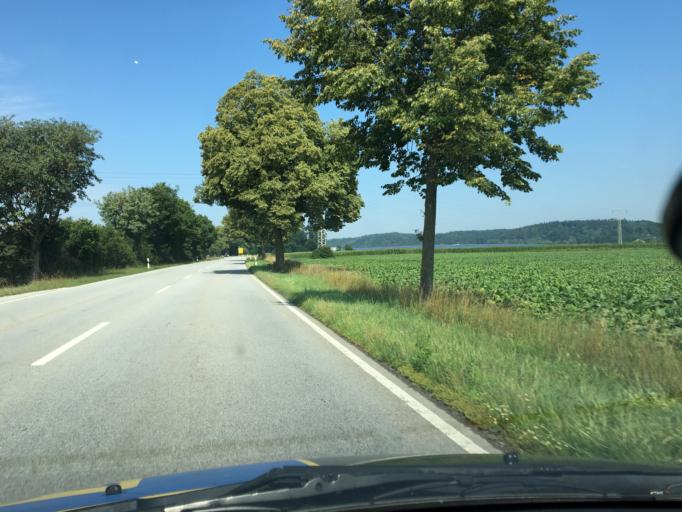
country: DE
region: Bavaria
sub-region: Upper Bavaria
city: Aresing
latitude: 48.2681
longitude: 12.6195
